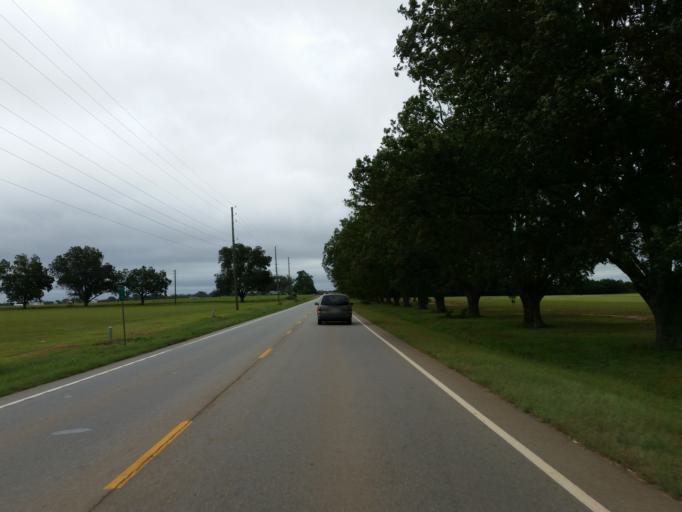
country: US
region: Georgia
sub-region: Peach County
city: Fort Valley
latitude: 32.5837
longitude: -83.9228
